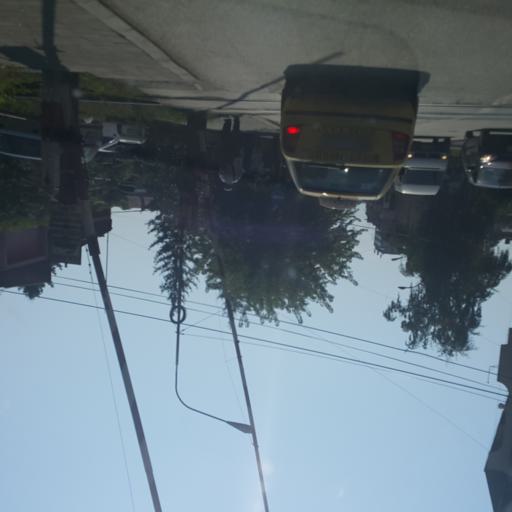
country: RS
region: Central Serbia
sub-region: Zajecarski Okrug
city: Zajecar
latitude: 43.9065
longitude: 22.2778
